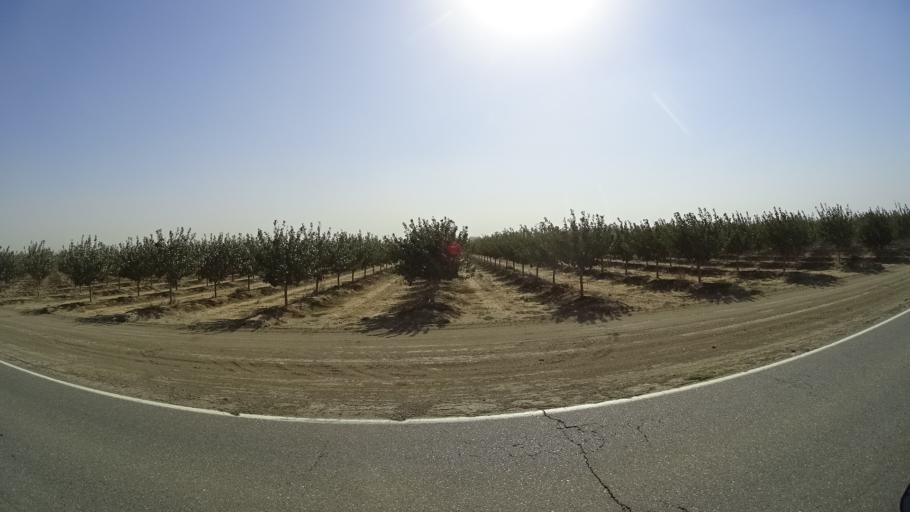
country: US
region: California
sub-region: Yolo County
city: Woodland
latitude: 38.7346
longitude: -121.7331
